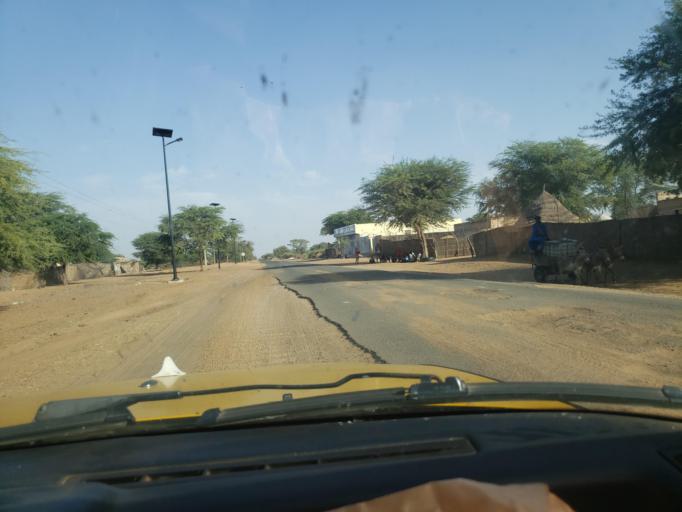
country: SN
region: Louga
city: Louga
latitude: 15.5111
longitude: -15.9862
